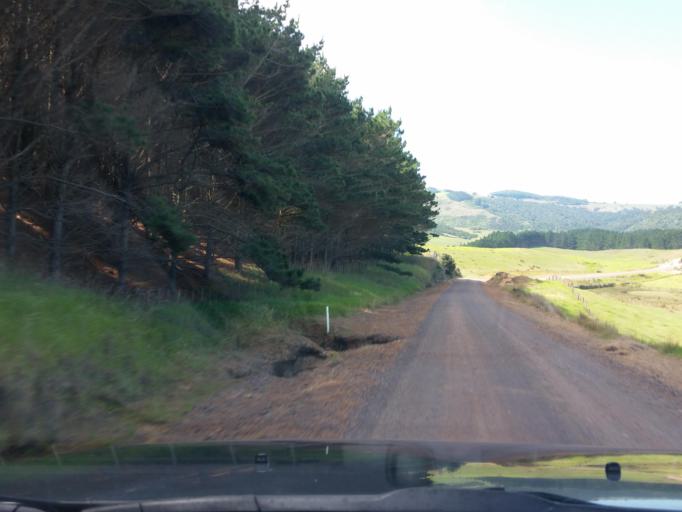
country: NZ
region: Northland
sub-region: Kaipara District
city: Dargaville
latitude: -35.7034
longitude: 173.5280
